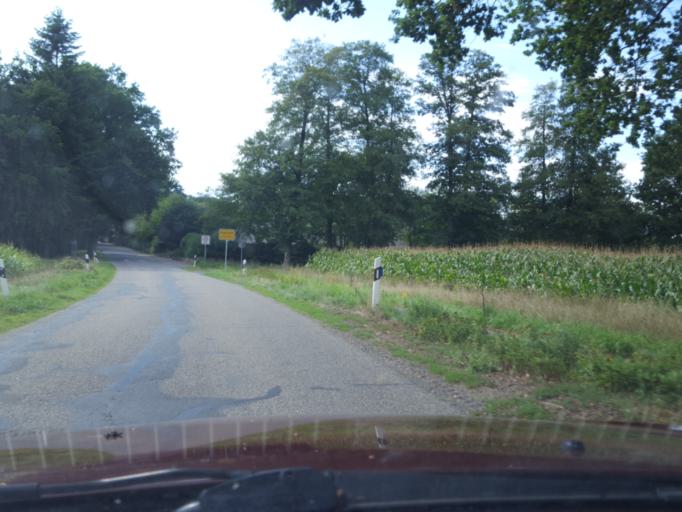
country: DE
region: Lower Saxony
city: Hemsbunde
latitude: 53.0783
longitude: 9.4592
